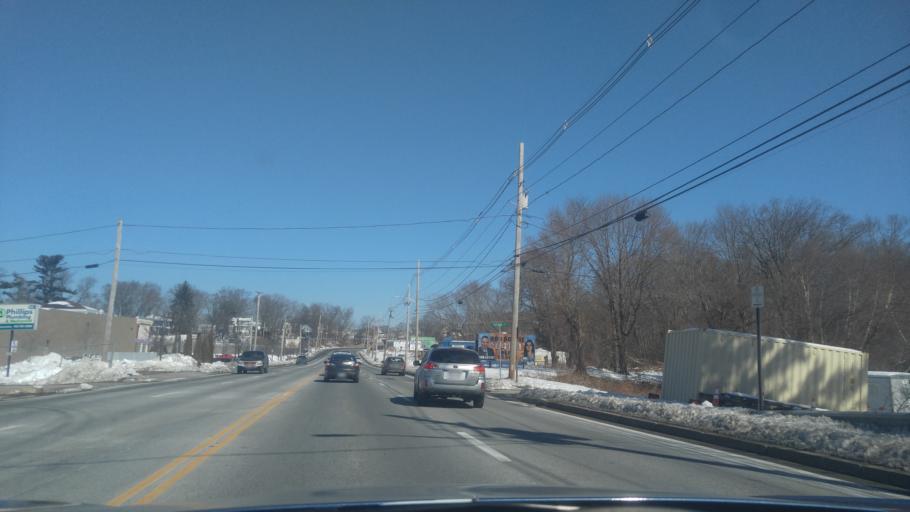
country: US
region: Rhode Island
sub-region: Providence County
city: Cranston
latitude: 41.7679
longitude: -71.4052
